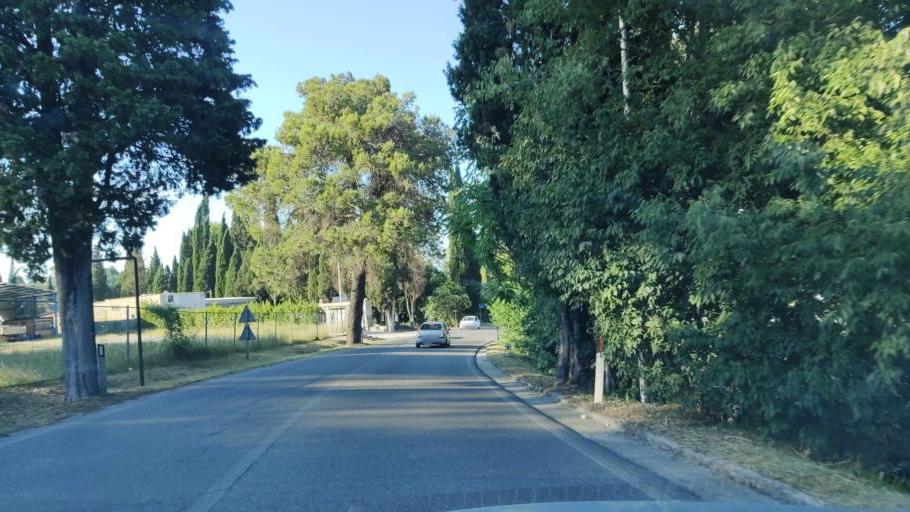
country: IT
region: Umbria
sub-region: Provincia di Terni
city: Narni Scalo
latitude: 42.5293
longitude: 12.5130
